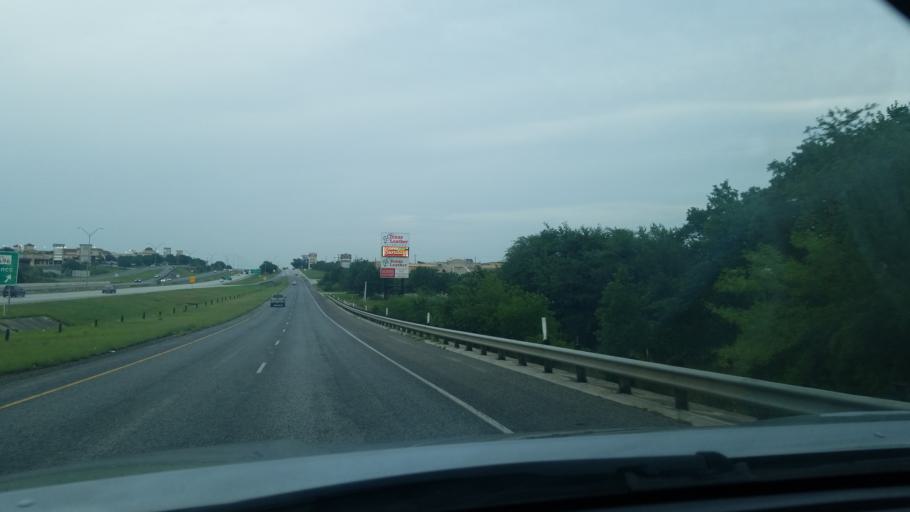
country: US
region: Texas
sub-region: Bexar County
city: Hollywood Park
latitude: 29.6081
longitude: -98.5194
